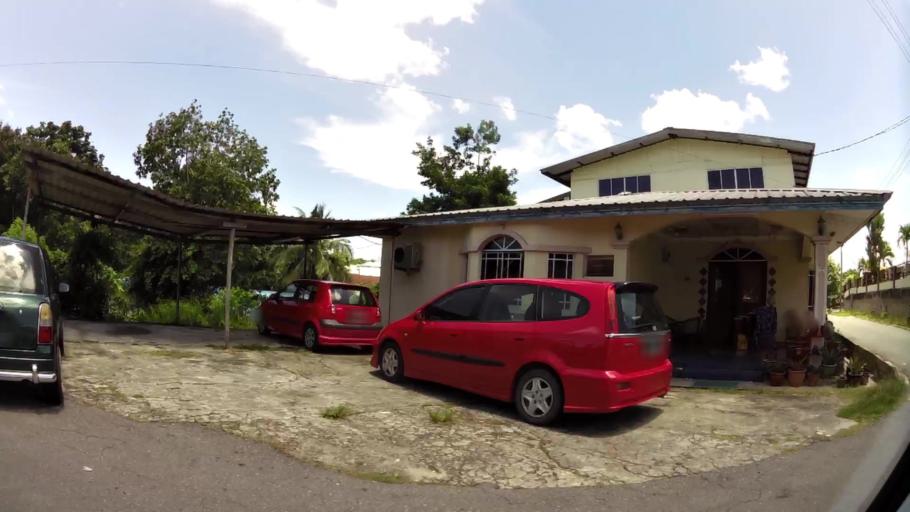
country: BN
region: Brunei and Muara
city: Bandar Seri Begawan
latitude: 4.9391
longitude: 114.9597
